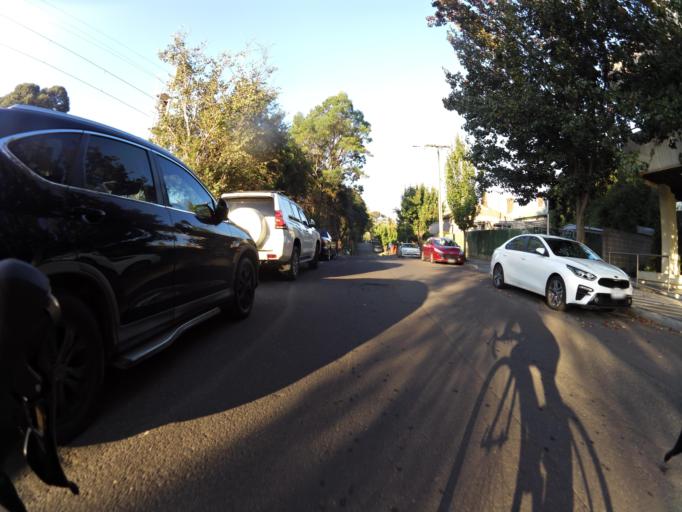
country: AU
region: Victoria
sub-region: Boroondara
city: Hawthorn East
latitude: -37.8230
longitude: 145.0479
